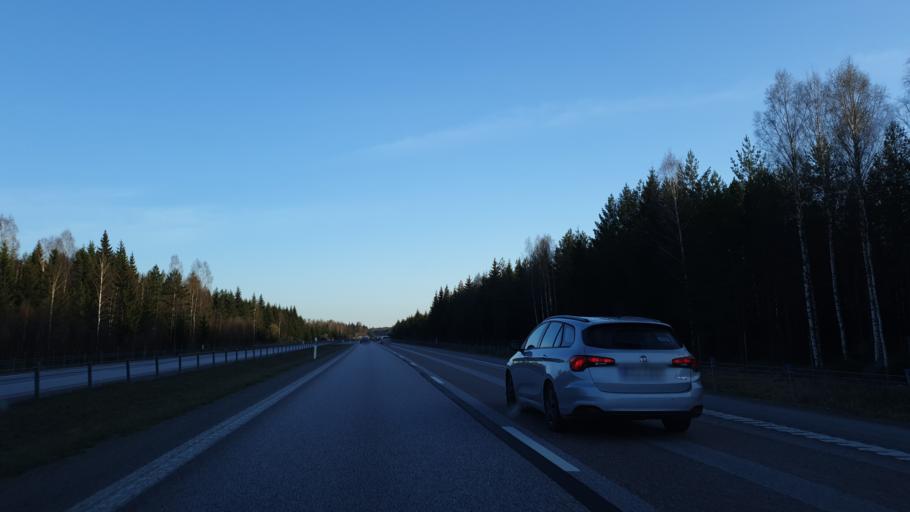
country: SE
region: Uppsala
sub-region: Tierps Kommun
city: Tierp
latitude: 60.2082
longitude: 17.4958
